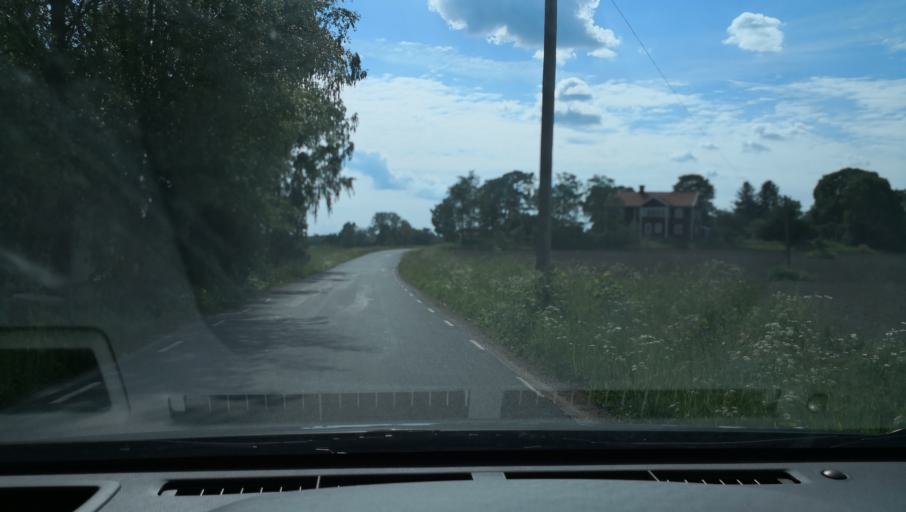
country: SE
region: Uppsala
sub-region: Enkopings Kommun
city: Orsundsbro
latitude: 59.8160
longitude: 17.3470
